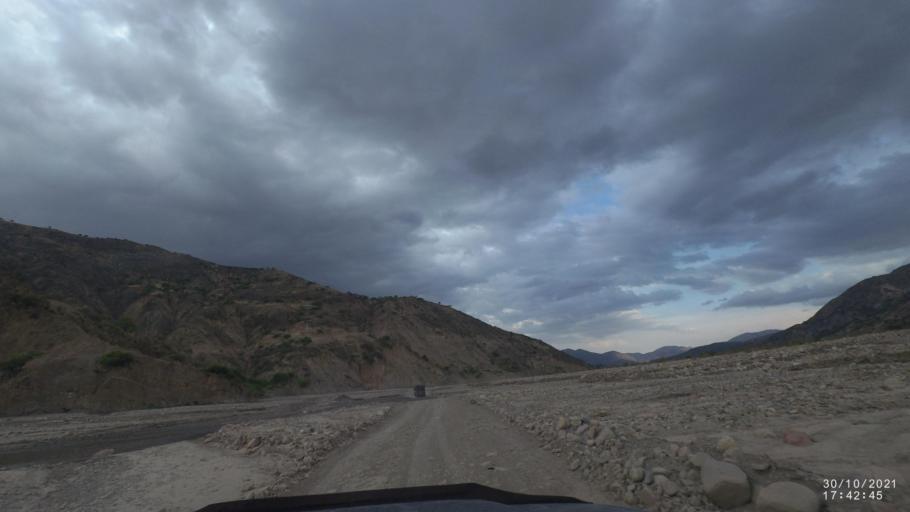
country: BO
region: Cochabamba
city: Sipe Sipe
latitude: -17.5257
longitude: -66.5416
